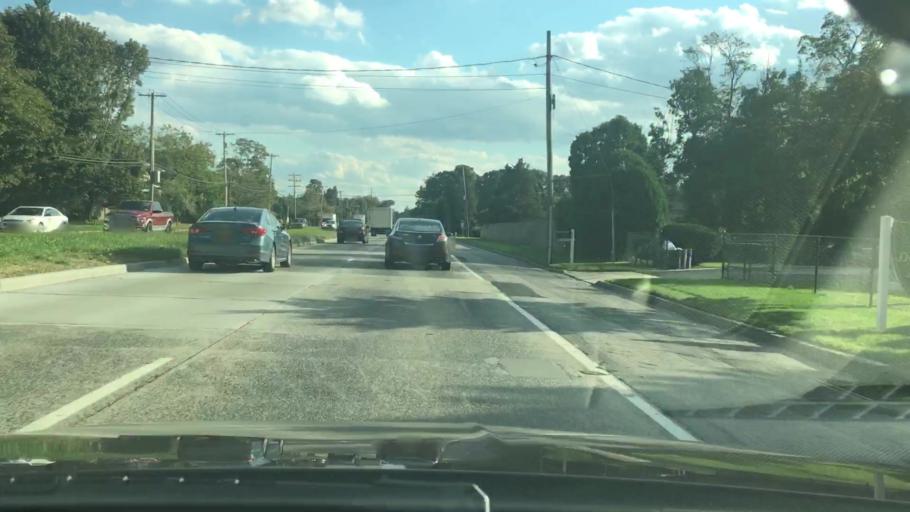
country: US
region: New York
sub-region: Suffolk County
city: Dix Hills
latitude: 40.7870
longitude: -73.3400
